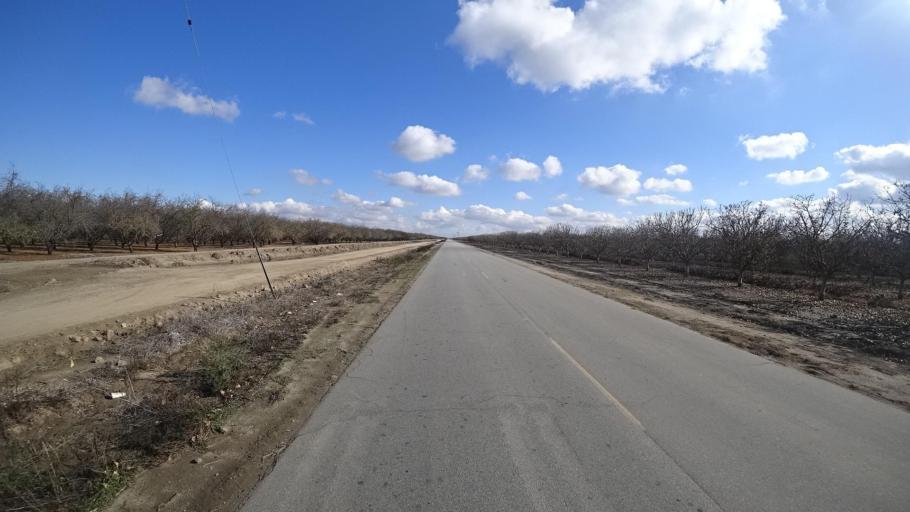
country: US
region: California
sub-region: Kern County
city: Wasco
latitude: 35.6742
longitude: -119.3253
